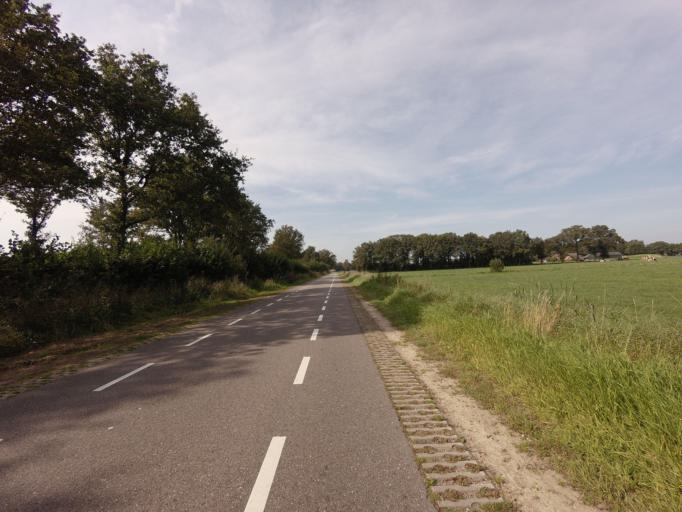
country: NL
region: Overijssel
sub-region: Gemeente Hof van Twente
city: Goor
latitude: 52.2624
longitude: 6.5723
